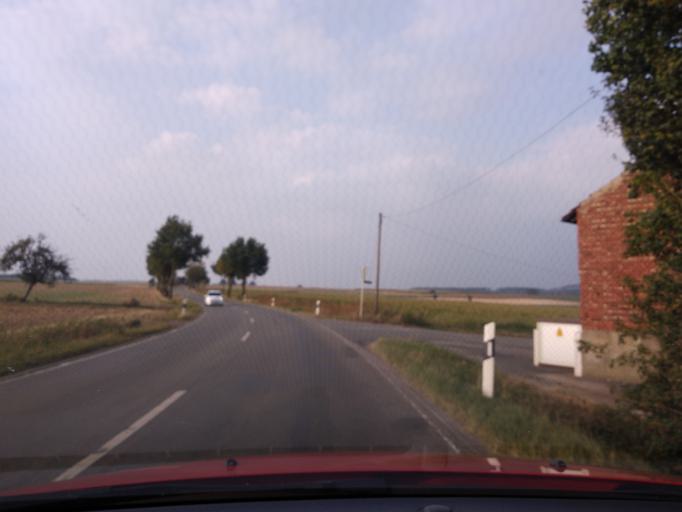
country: DE
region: Hesse
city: Liebenau
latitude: 51.5482
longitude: 9.2962
